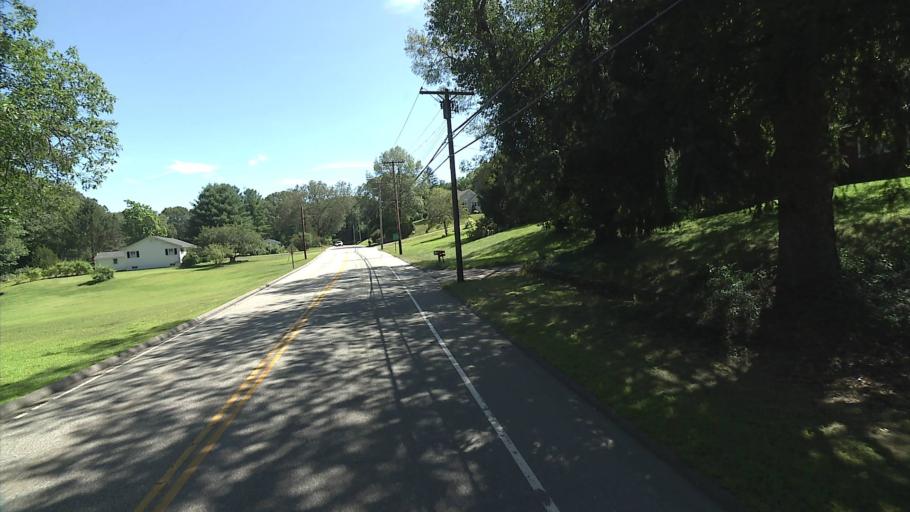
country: US
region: Connecticut
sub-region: New London County
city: Baltic
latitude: 41.6024
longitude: -72.0564
